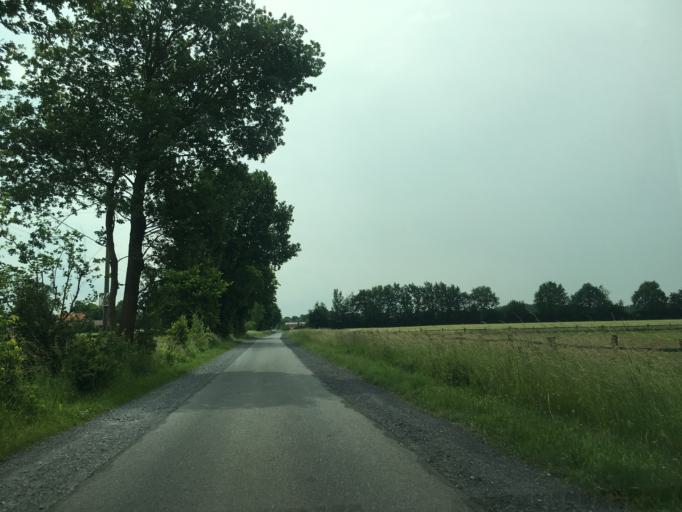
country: DE
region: North Rhine-Westphalia
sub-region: Regierungsbezirk Munster
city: Muenster
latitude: 52.0165
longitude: 7.6326
